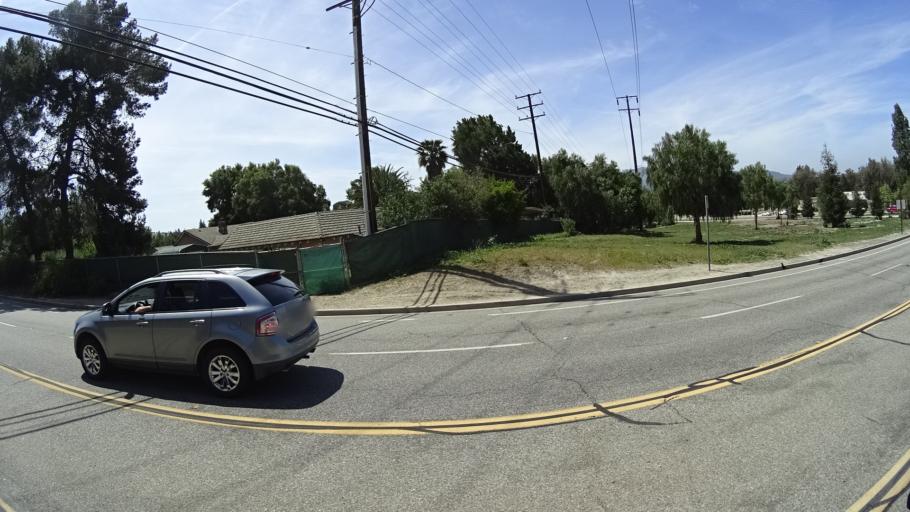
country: US
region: California
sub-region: Ventura County
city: Thousand Oaks
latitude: 34.1994
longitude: -118.8513
